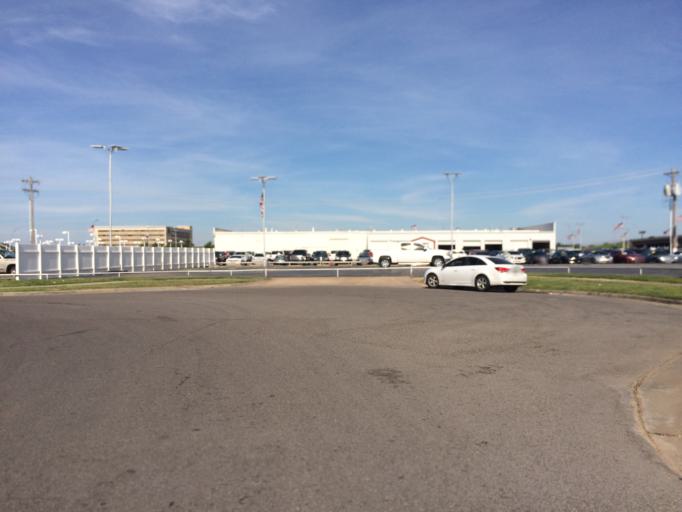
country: US
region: Oklahoma
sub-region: Cleveland County
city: Norman
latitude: 35.2316
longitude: -97.4826
